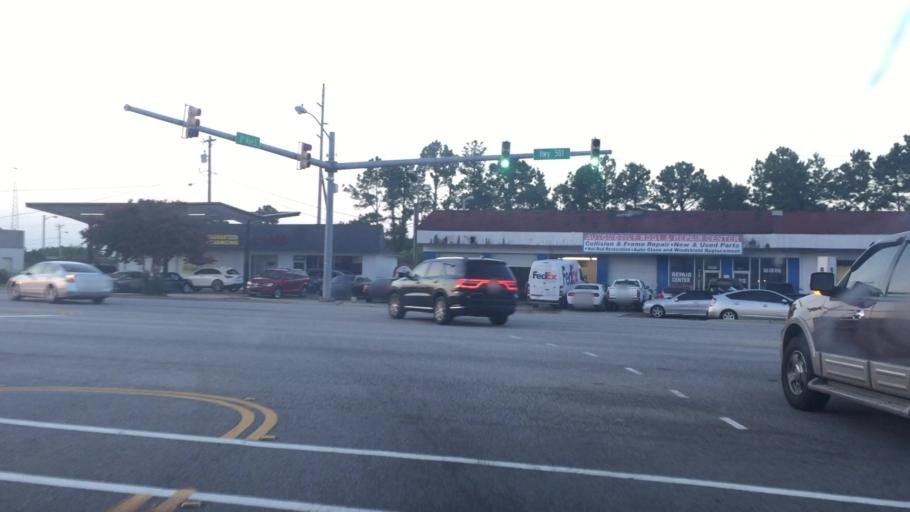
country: US
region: South Carolina
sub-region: Horry County
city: Myrtle Beach
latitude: 33.6988
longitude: -78.8994
